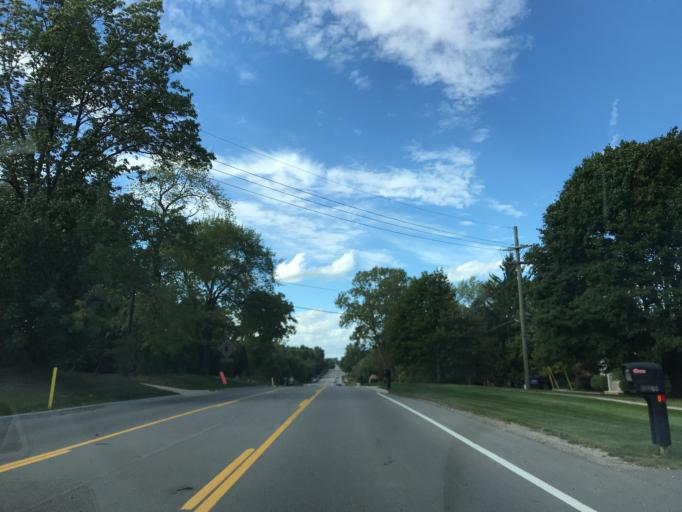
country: US
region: Michigan
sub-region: Oakland County
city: Farmington Hills
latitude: 42.5144
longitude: -83.3986
